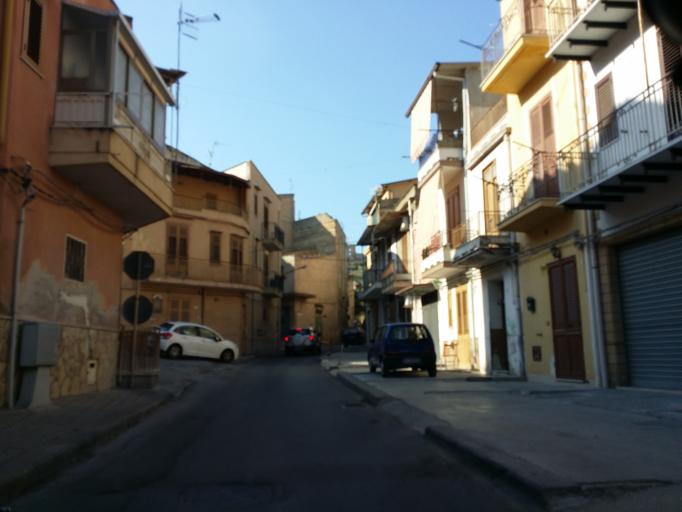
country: IT
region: Sicily
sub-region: Palermo
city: Misilmeri
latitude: 38.0304
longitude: 13.4478
